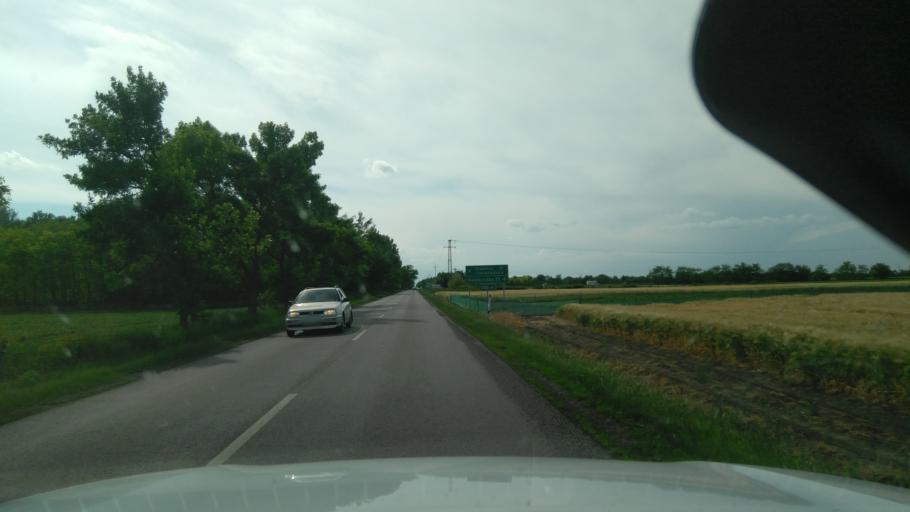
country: HU
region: Bekes
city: Medgyesegyhaza
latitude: 46.5133
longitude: 20.9781
